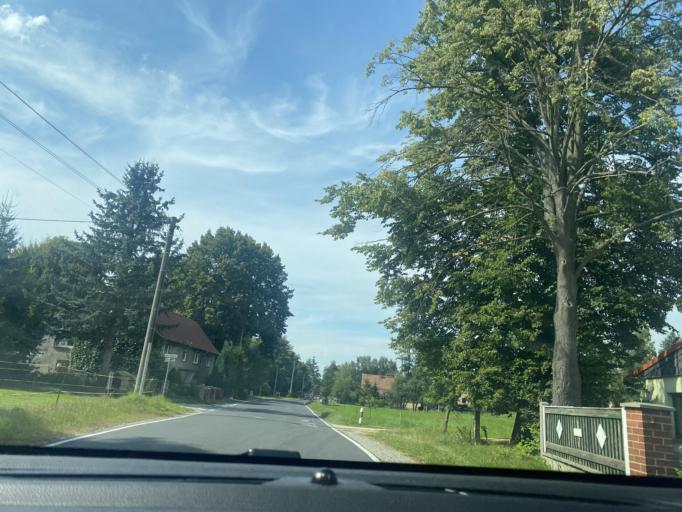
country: DE
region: Saxony
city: Sohland am Rotstein
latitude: 51.1222
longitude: 14.7867
